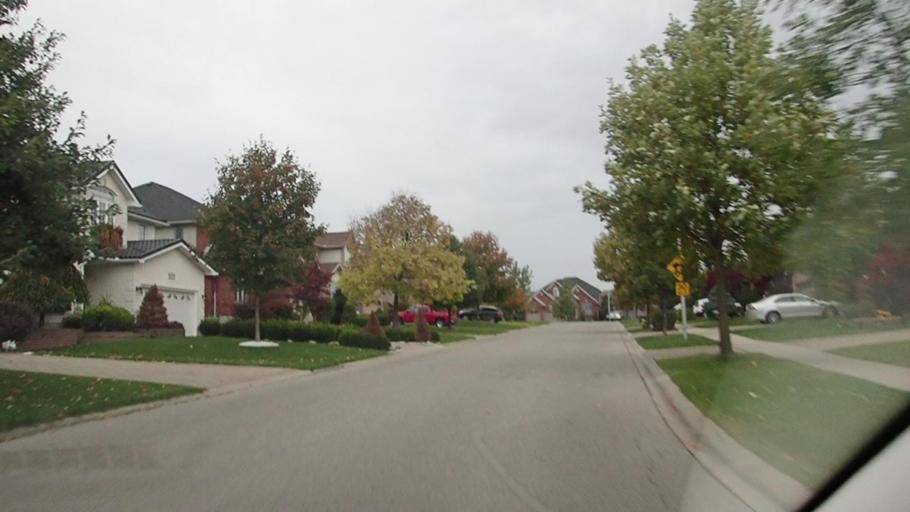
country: CA
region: Ontario
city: London
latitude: 43.0389
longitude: -81.2710
